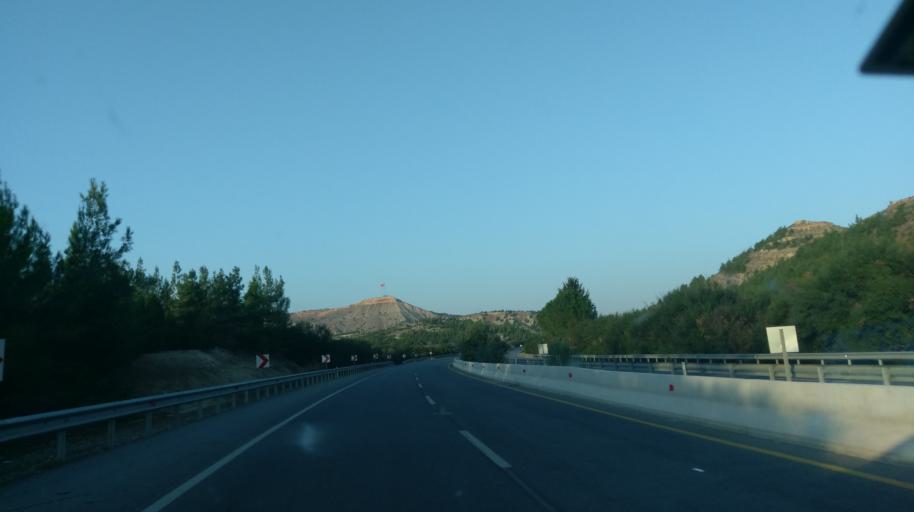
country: CY
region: Lefkosia
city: Akaki
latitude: 35.2027
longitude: 33.1161
